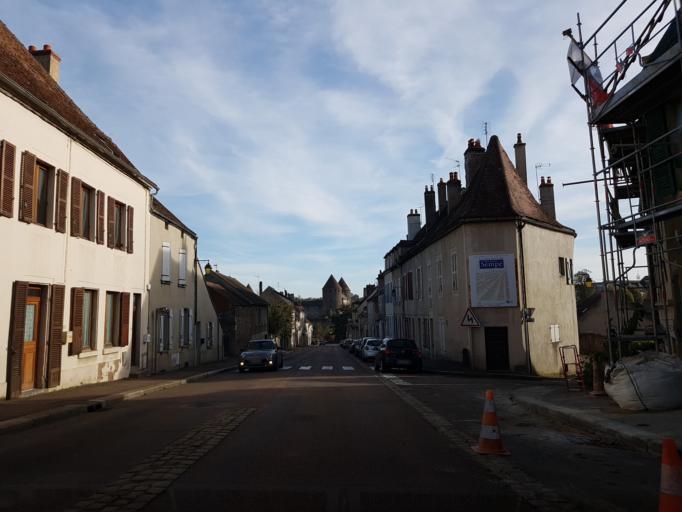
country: FR
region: Bourgogne
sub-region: Departement de la Cote-d'Or
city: Semur-en-Auxois
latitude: 47.4932
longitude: 4.3262
